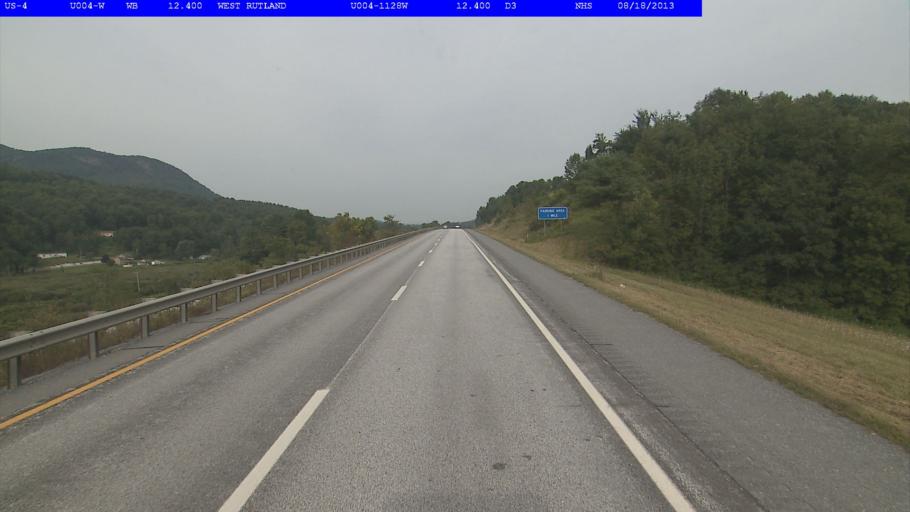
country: US
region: Vermont
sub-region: Rutland County
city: West Rutland
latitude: 43.6073
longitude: -73.0769
